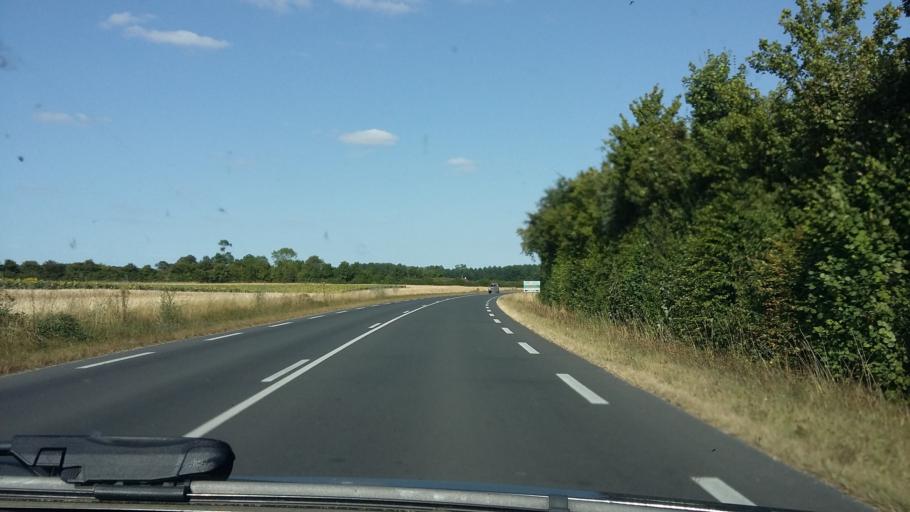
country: FR
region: Poitou-Charentes
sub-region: Departement de la Charente-Maritime
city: Matha
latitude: 45.8774
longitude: -0.3216
